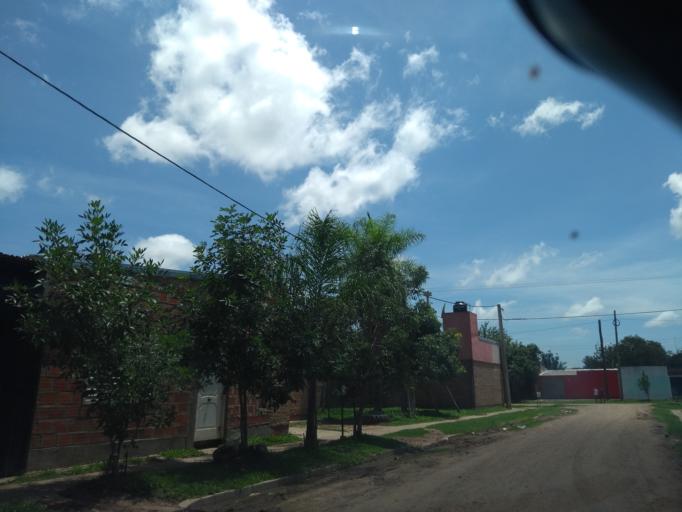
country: AR
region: Chaco
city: Resistencia
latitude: -27.4607
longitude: -58.9626
